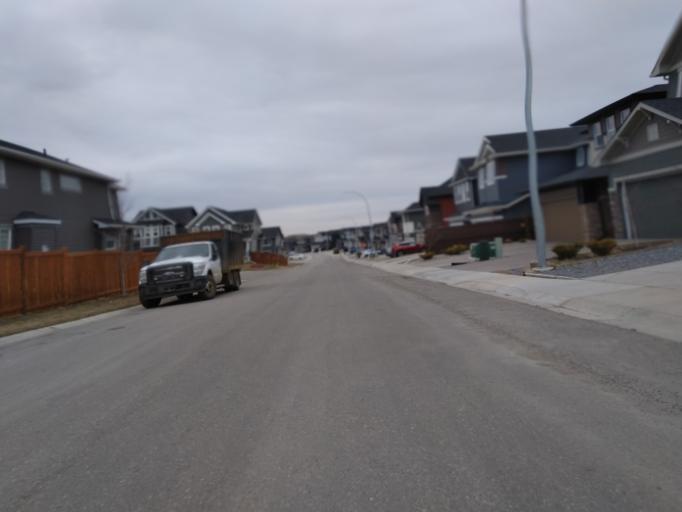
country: CA
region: Alberta
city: Calgary
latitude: 51.1764
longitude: -114.0975
